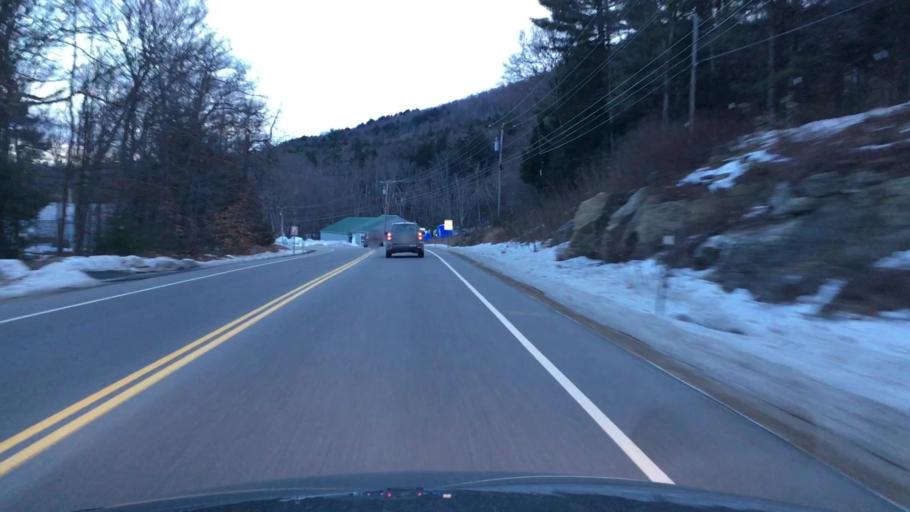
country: US
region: New Hampshire
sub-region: Merrimack County
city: Newbury
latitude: 43.3251
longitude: -72.0425
